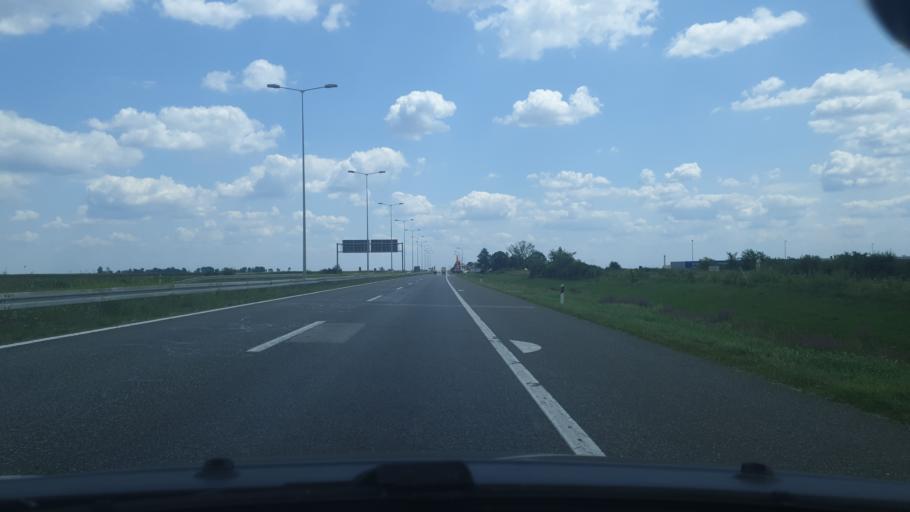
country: RS
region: Autonomna Pokrajina Vojvodina
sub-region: Sremski Okrug
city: Ruma
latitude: 44.9604
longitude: 19.8161
